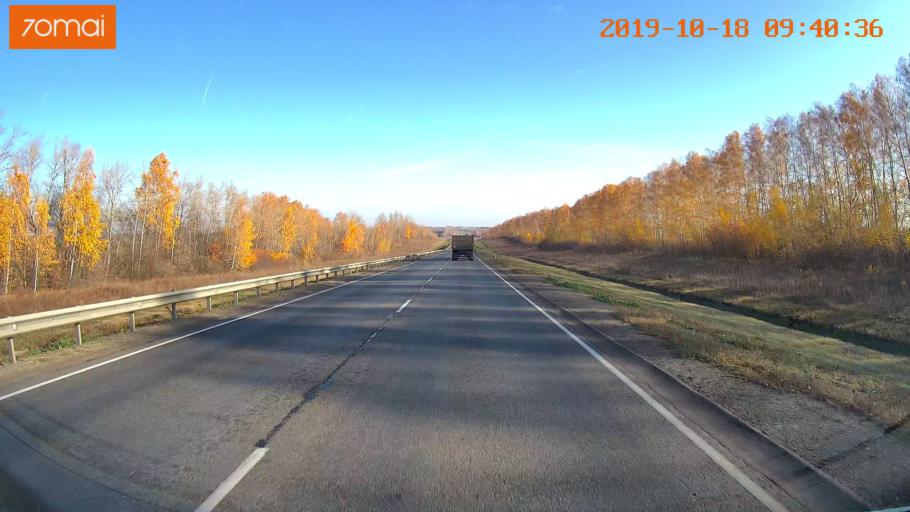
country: RU
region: Tula
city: Kazachka
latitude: 53.2659
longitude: 38.1504
